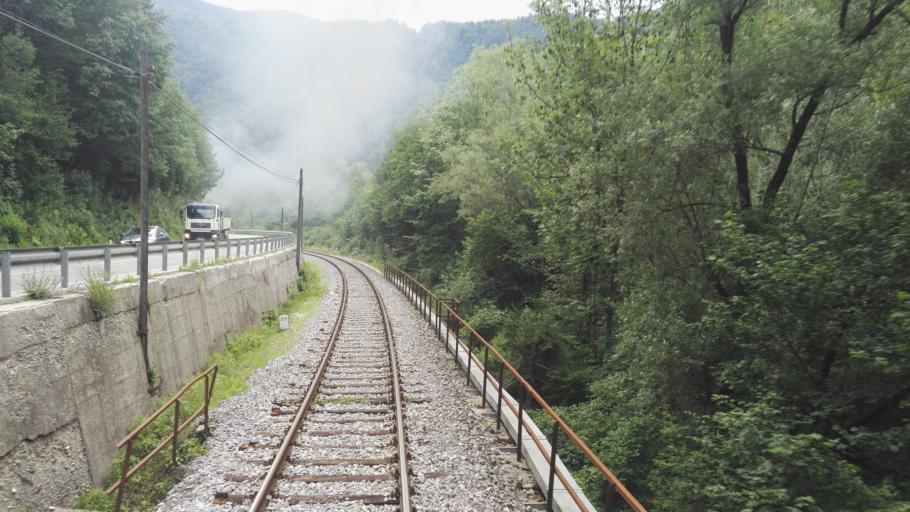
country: SI
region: Bohinj
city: Bohinjska Bistrica
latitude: 46.2853
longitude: 14.0175
